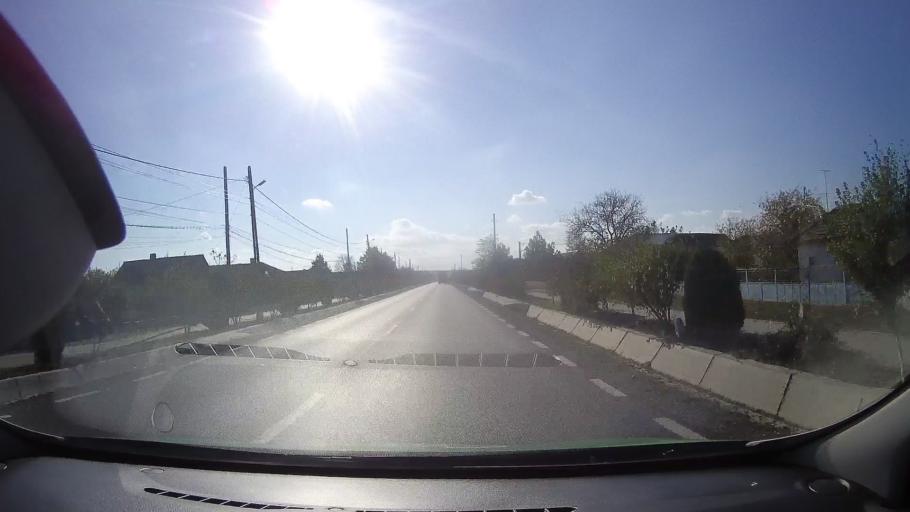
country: RO
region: Tulcea
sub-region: Comuna Baia
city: Baia
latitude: 44.7307
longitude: 28.6816
